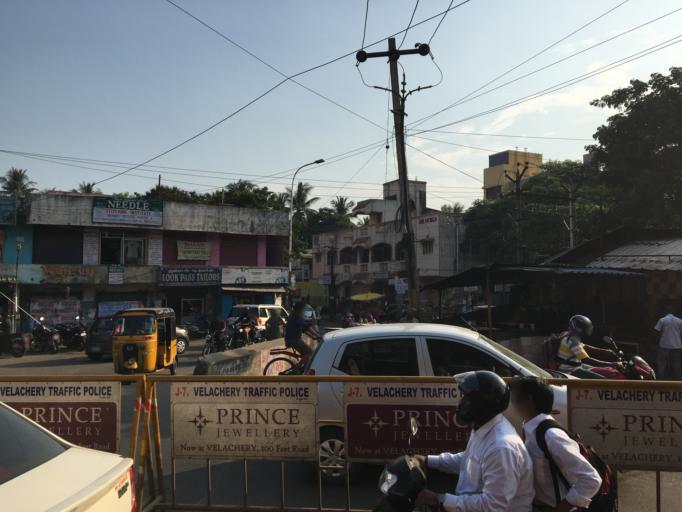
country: IN
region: Tamil Nadu
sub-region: Kancheepuram
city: Perungudi
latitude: 12.9758
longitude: 80.2204
